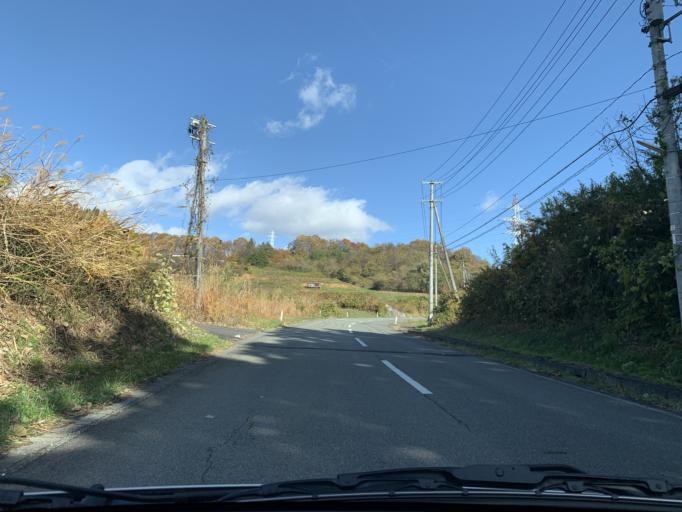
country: JP
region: Iwate
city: Mizusawa
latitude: 39.0272
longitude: 141.1078
